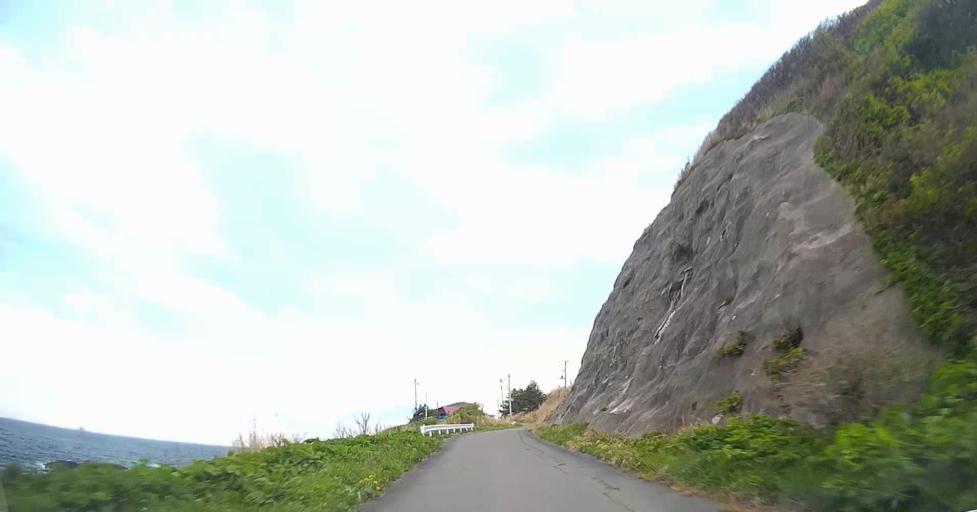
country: JP
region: Aomori
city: Shimokizukuri
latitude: 41.2422
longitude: 140.3424
